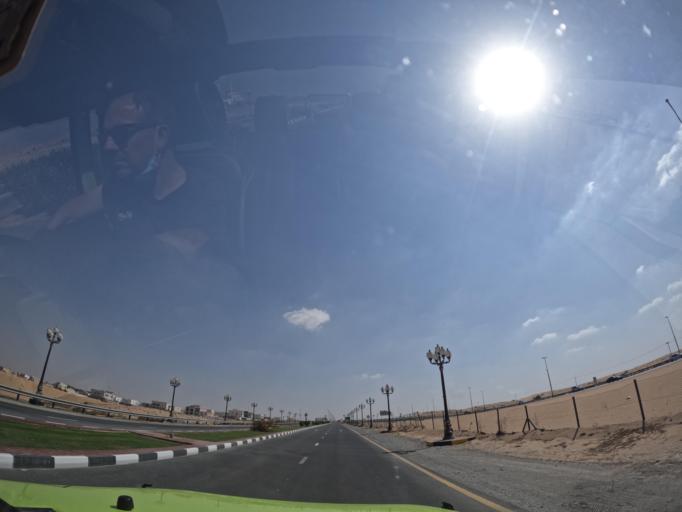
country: AE
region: Ash Shariqah
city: Sharjah
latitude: 25.2354
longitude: 55.5769
